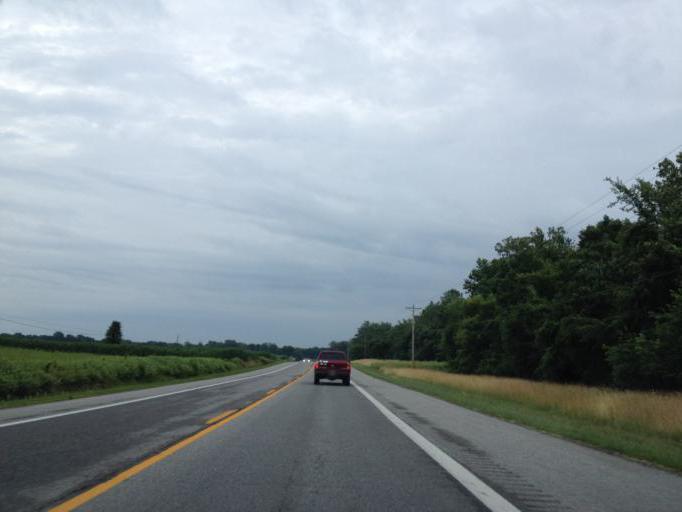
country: US
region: Maryland
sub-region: Caroline County
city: Ridgely
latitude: 38.9257
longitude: -75.9887
